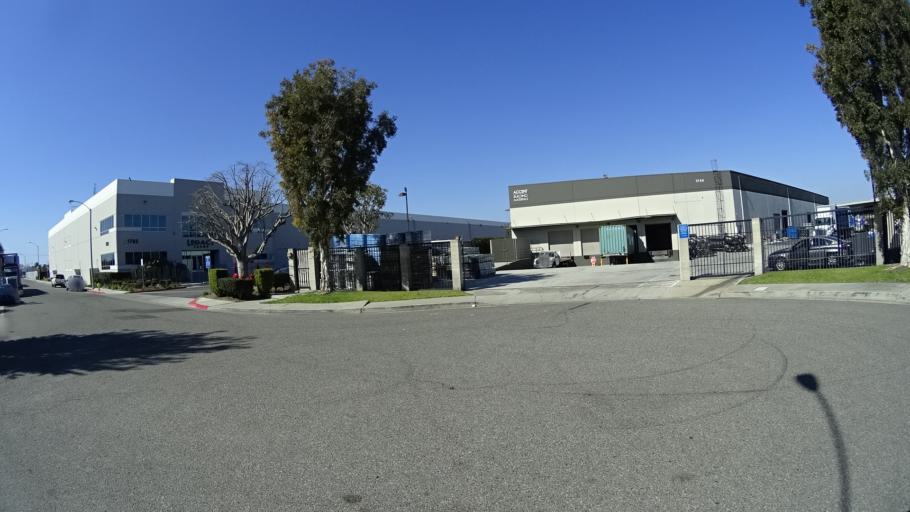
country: US
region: California
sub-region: Orange County
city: Anaheim
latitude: 33.8351
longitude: -117.9444
